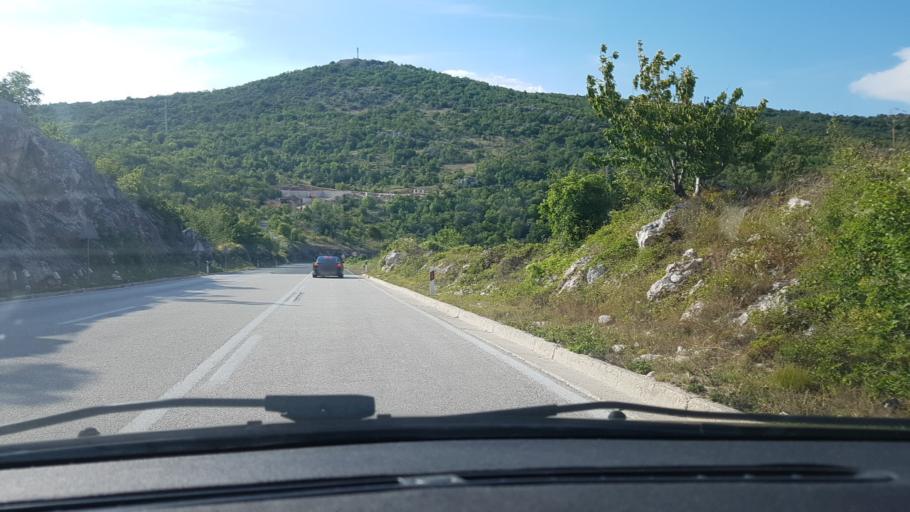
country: HR
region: Splitsko-Dalmatinska
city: Grubine
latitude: 43.4169
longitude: 17.1085
